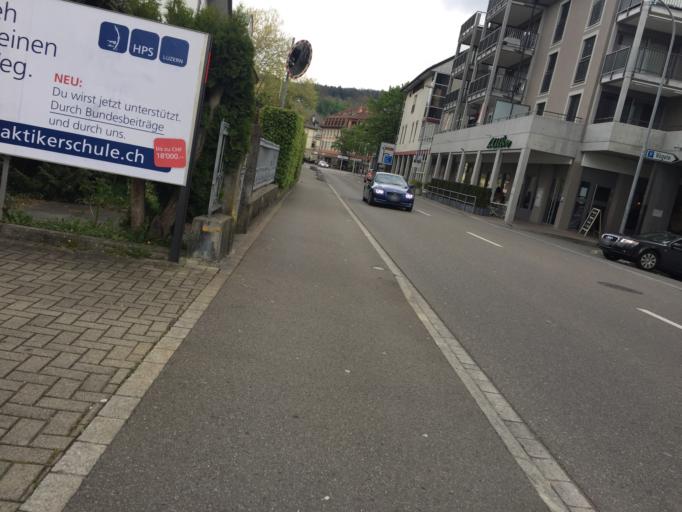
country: CH
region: Aargau
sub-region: Bezirk Brugg
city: Brugg
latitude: 47.4821
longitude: 8.2074
